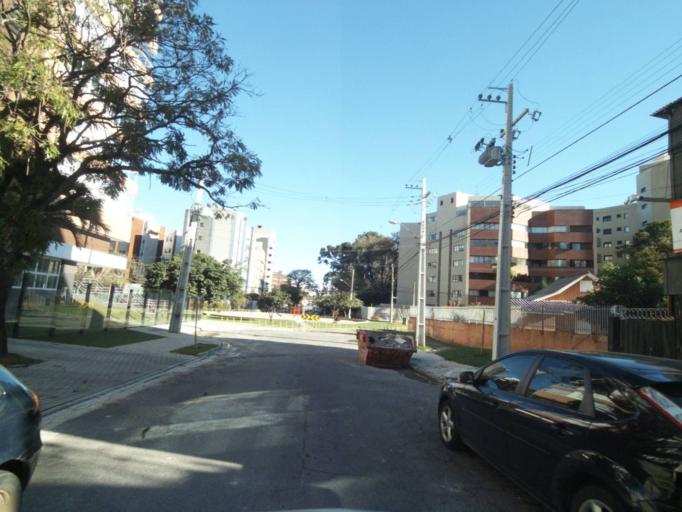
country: BR
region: Parana
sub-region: Curitiba
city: Curitiba
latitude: -25.4142
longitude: -49.2557
